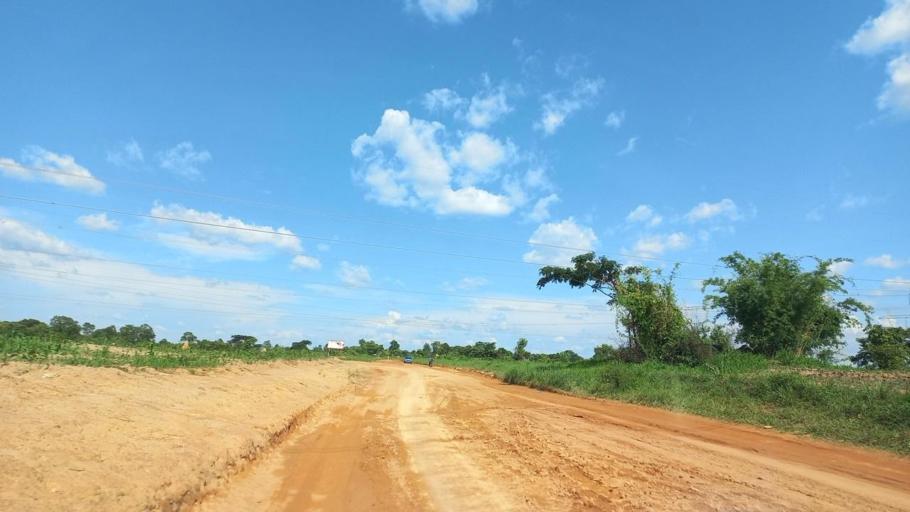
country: ZM
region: Copperbelt
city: Kitwe
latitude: -12.8710
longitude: 28.3440
